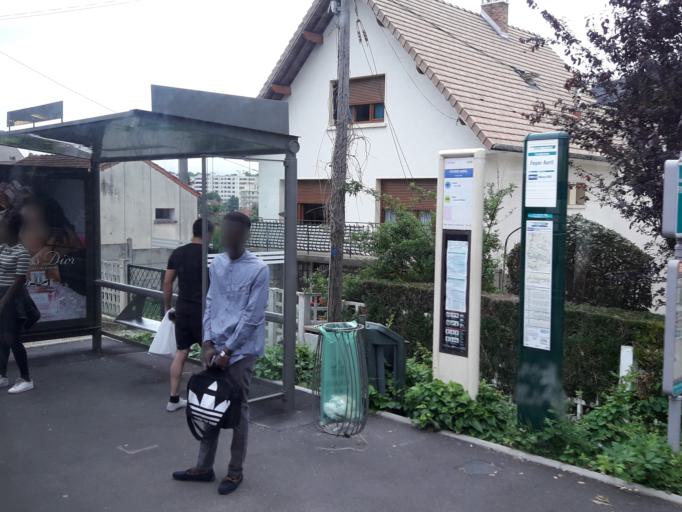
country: FR
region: Ile-de-France
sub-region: Departement de l'Essonne
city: Longjumeau
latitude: 48.6919
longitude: 2.2979
